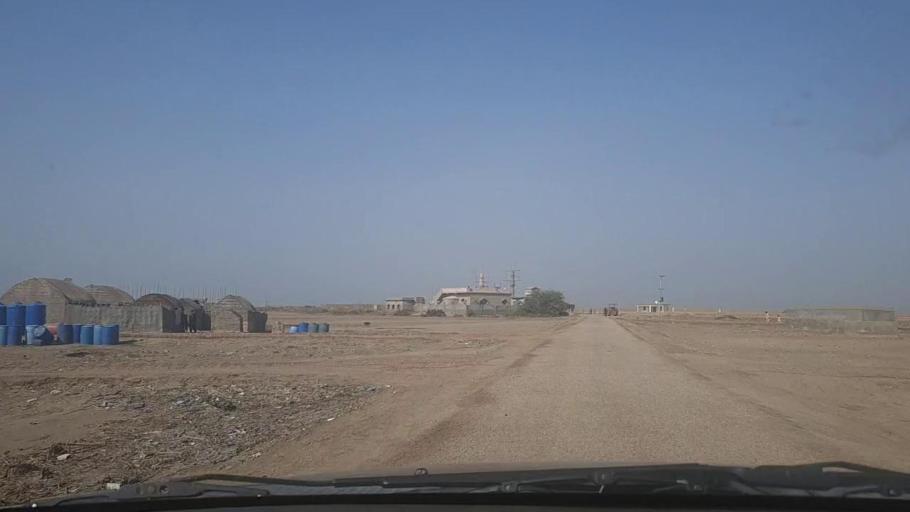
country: PK
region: Sindh
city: Keti Bandar
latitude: 24.1821
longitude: 67.5024
